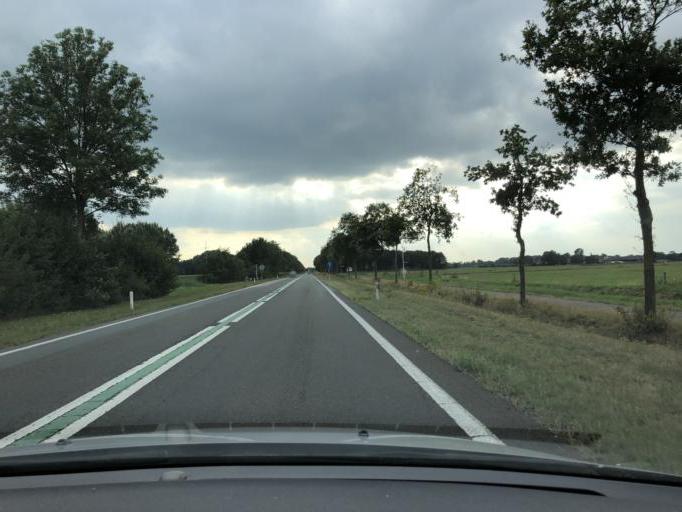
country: NL
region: Drenthe
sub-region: Gemeente Hoogeveen
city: Hoogeveen
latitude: 52.6131
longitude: 6.5052
